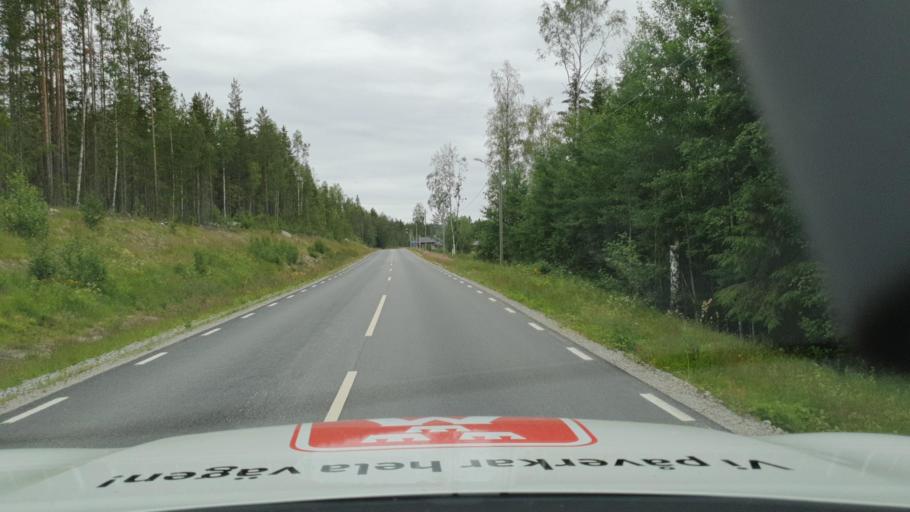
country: SE
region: Vaesterbotten
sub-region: Nordmalings Kommun
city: Nordmaling
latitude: 63.5208
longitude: 19.3602
